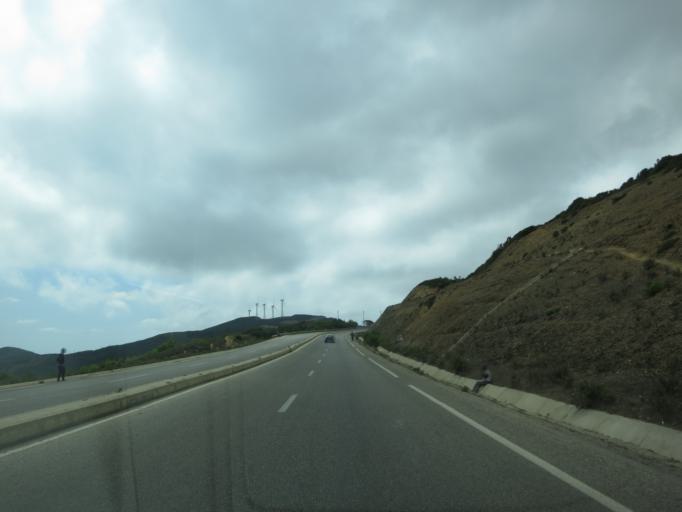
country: ES
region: Ceuta
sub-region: Ceuta
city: Ceuta
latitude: 35.8617
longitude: -5.4228
